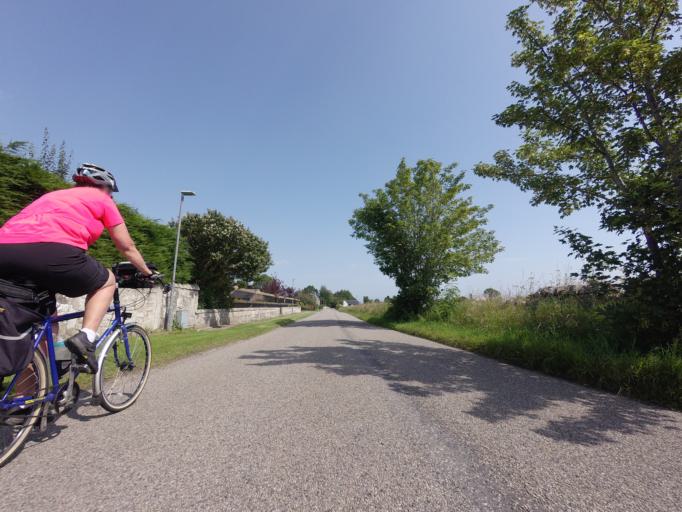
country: GB
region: Scotland
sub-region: Highland
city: Tain
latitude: 57.8023
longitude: -4.0661
